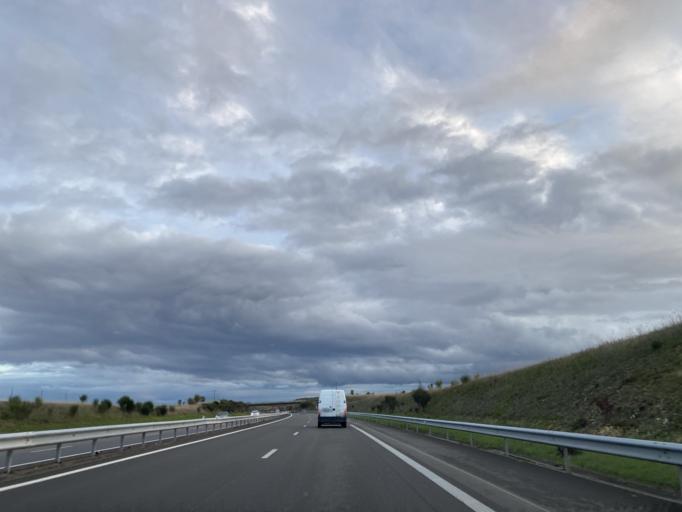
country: FR
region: Centre
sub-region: Departement du Cher
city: Trouy
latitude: 47.0133
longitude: 2.3839
